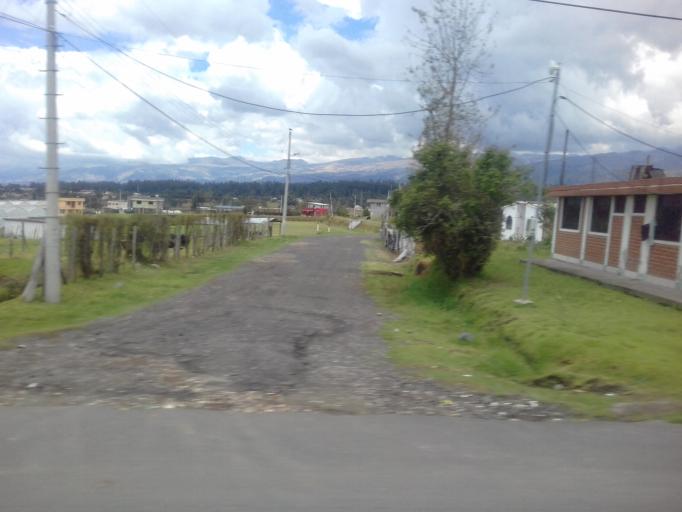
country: EC
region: Pichincha
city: Sangolqui
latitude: -0.3419
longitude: -78.4127
